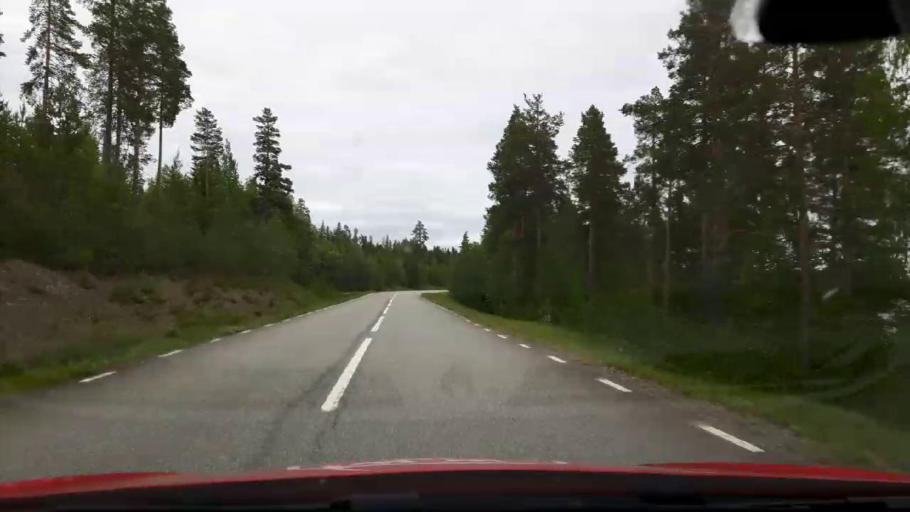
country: SE
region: Jaemtland
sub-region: Stroemsunds Kommun
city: Stroemsund
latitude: 63.3726
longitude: 15.6984
